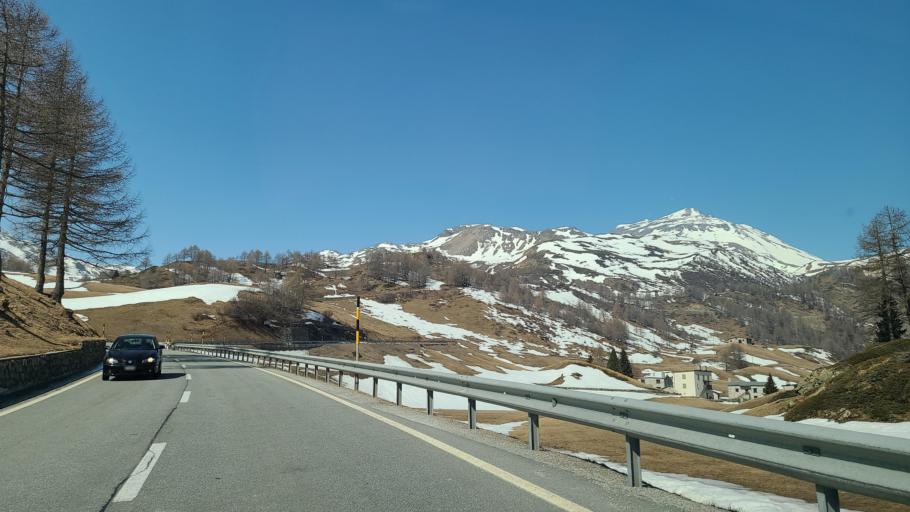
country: CH
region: Grisons
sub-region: Bernina District
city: Poschiavo
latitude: 46.4090
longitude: 10.0586
